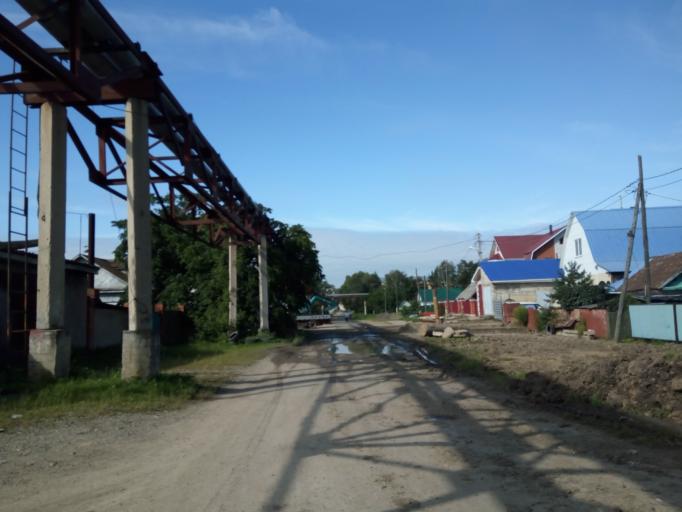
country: RU
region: Primorskiy
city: Dal'nerechensk
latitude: 45.9342
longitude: 133.7409
